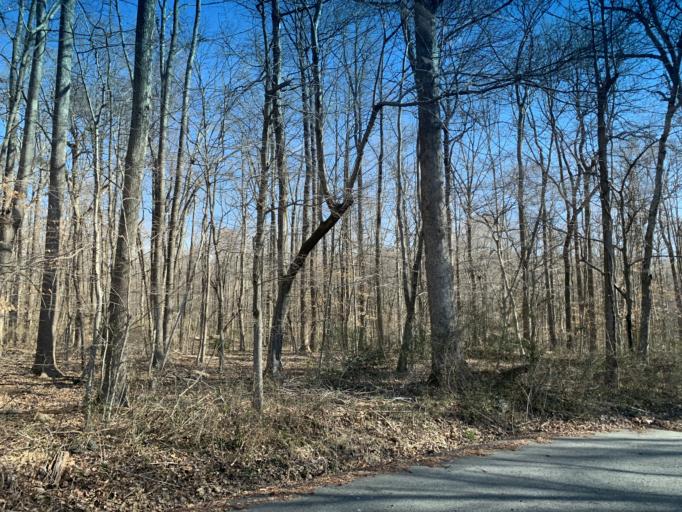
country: US
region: Maryland
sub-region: Harford County
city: Aberdeen
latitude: 39.5410
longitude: -76.2204
